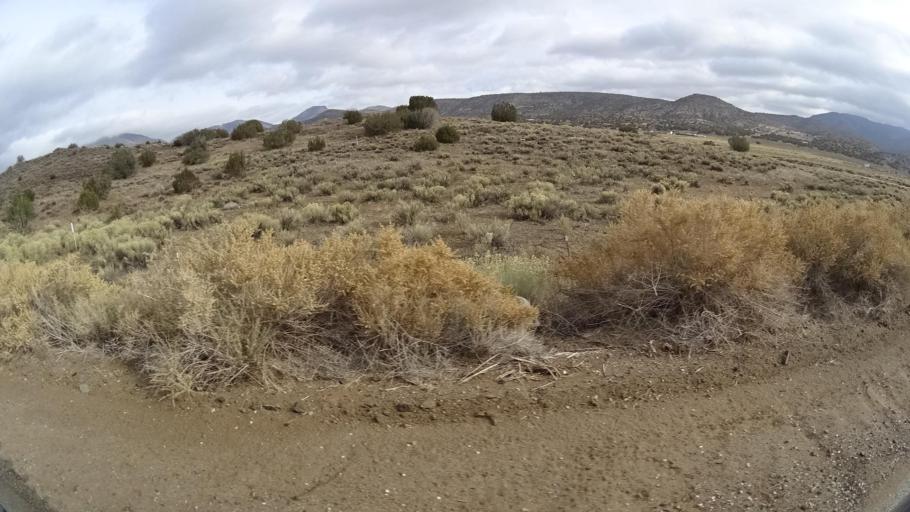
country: US
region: California
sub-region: Kern County
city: Tehachapi
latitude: 35.1662
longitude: -118.3330
